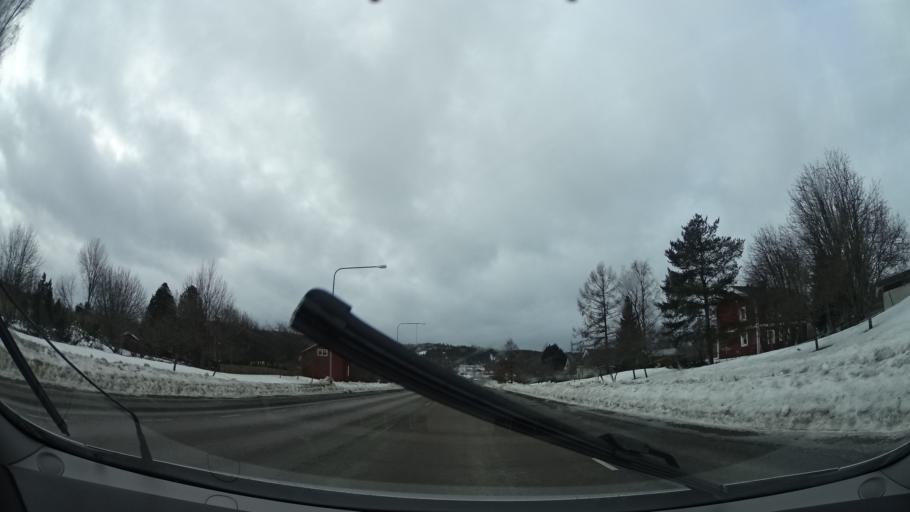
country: SE
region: Vaesterbotten
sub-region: Skelleftea Kommun
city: Skelleftea
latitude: 64.7481
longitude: 21.0161
